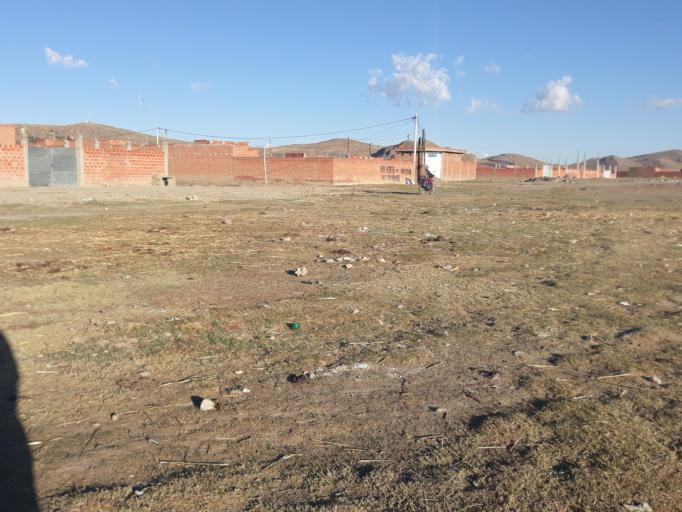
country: BO
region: La Paz
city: Achacachi
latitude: -16.0516
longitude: -68.6878
